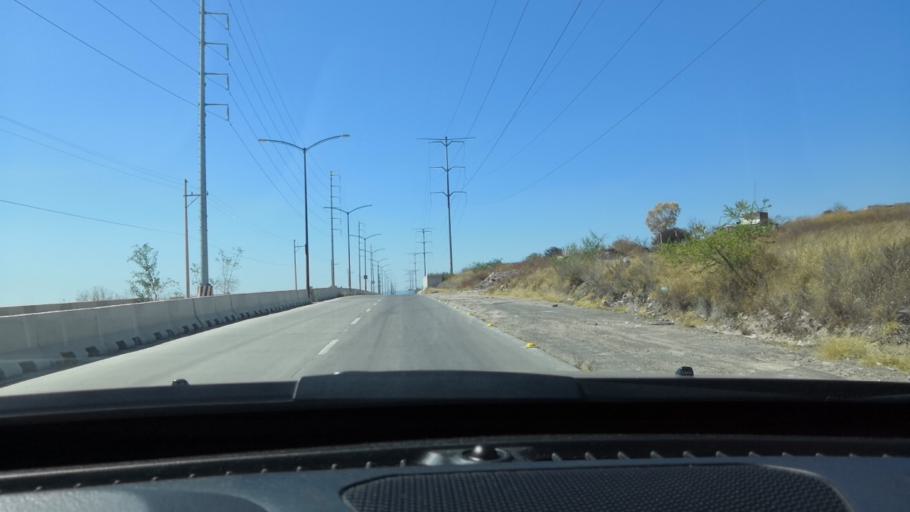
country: MX
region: Guanajuato
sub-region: Leon
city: Centro Familiar la Soledad
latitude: 21.1177
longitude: -101.7466
